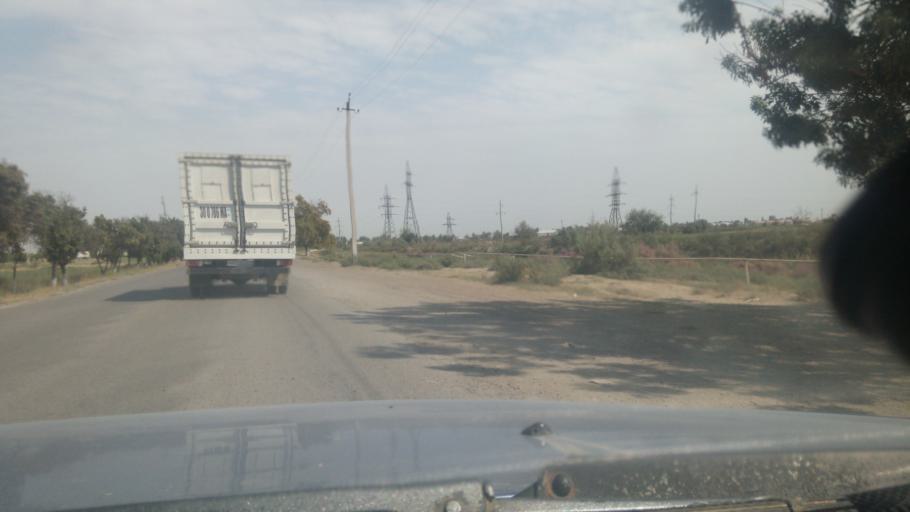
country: UZ
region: Sirdaryo
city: Guliston
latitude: 40.5329
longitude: 68.7621
